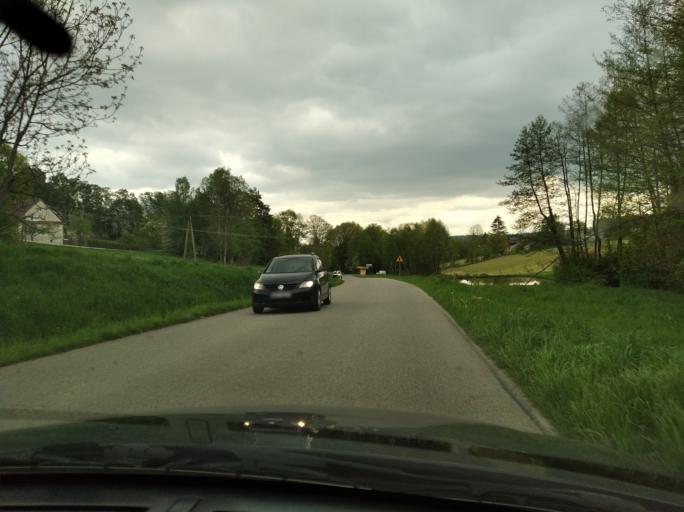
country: PL
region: Subcarpathian Voivodeship
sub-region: Powiat debicki
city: Leki Gorne
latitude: 49.9794
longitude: 21.1582
